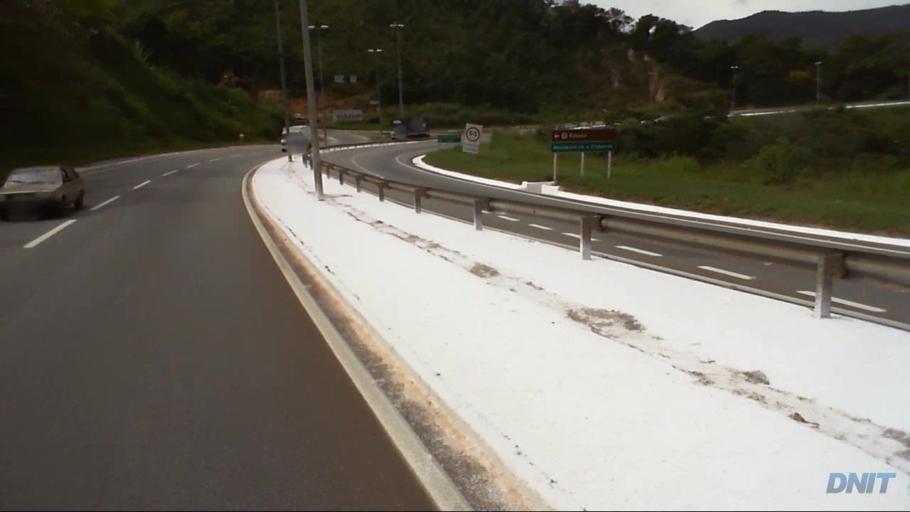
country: BR
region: Minas Gerais
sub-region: Santa Luzia
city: Santa Luzia
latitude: -19.7985
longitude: -43.7557
